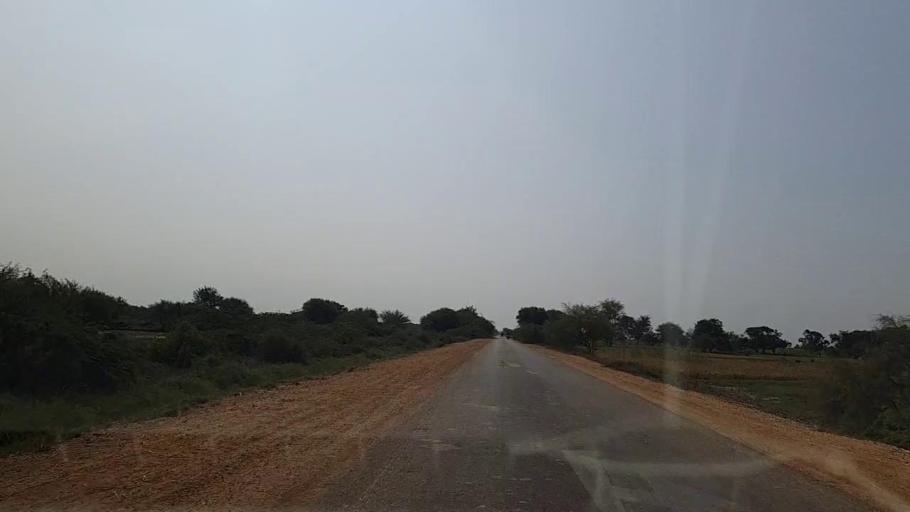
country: PK
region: Sindh
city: Chuhar Jamali
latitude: 24.2744
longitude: 67.9152
